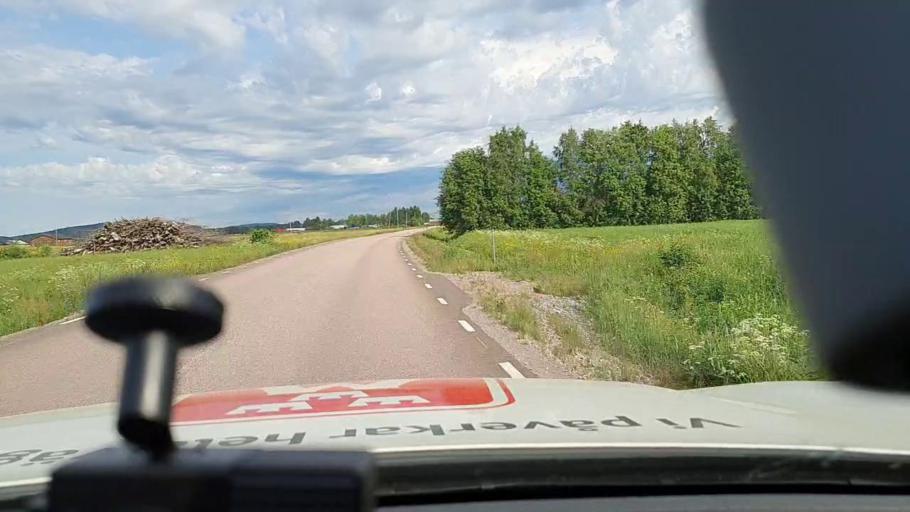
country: SE
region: Norrbotten
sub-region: Bodens Kommun
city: Saevast
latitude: 65.6990
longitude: 21.7735
